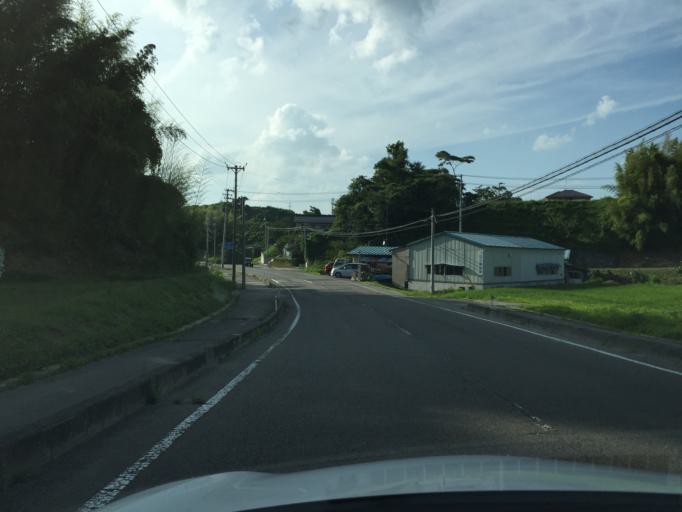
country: JP
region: Fukushima
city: Miharu
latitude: 37.4310
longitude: 140.4968
